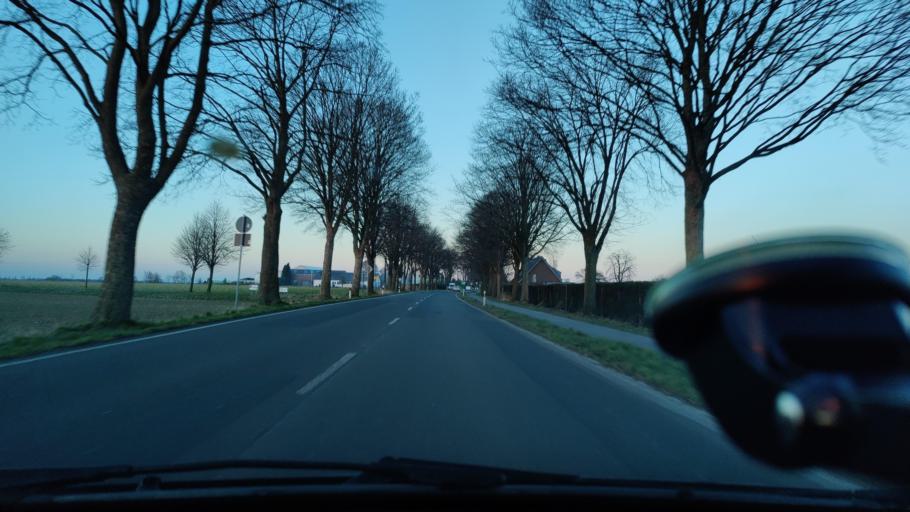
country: DE
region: North Rhine-Westphalia
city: Kalkar
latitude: 51.7136
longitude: 6.2524
